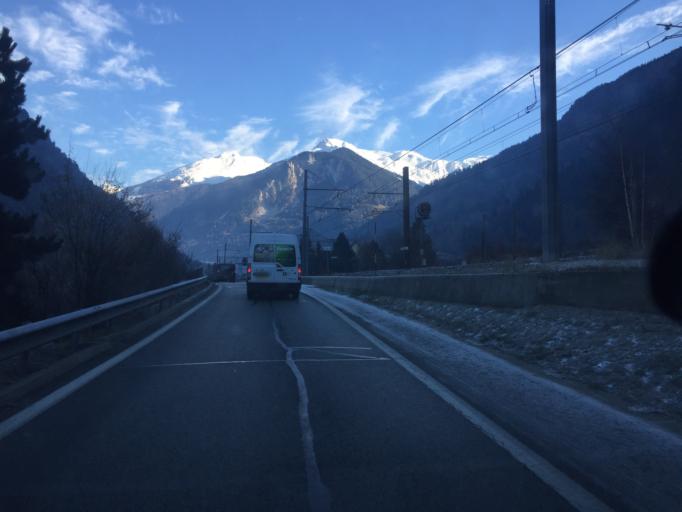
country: FR
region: Rhone-Alpes
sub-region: Departement de la Savoie
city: Modane
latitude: 45.1956
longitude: 6.6227
